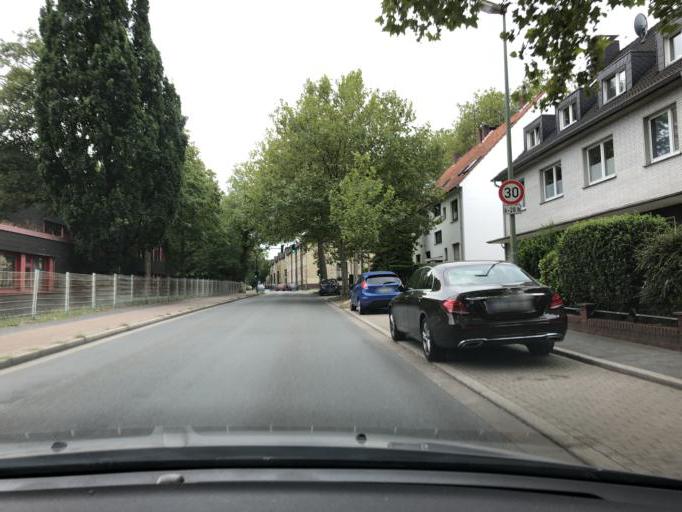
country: DE
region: North Rhine-Westphalia
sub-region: Regierungsbezirk Munster
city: Bottrop
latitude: 51.4756
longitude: 6.9421
